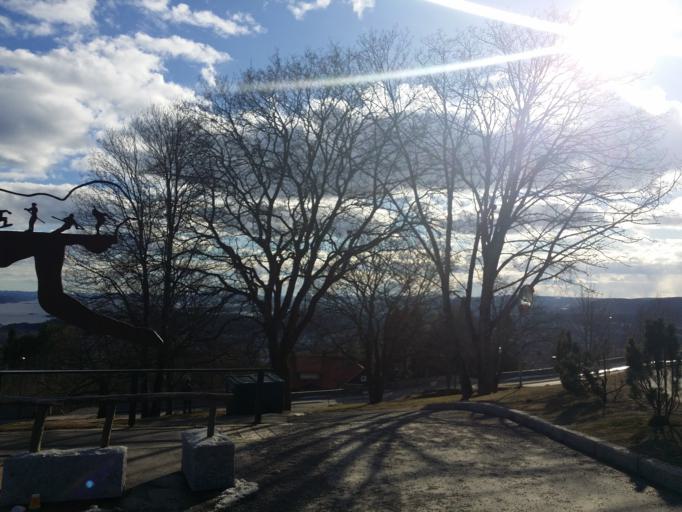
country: NO
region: Oslo
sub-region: Oslo
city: Sjolyststranda
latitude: 59.9606
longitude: 10.6663
